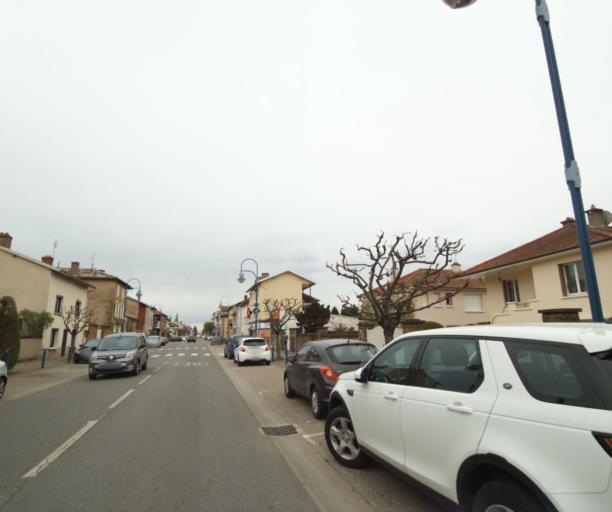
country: FR
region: Bourgogne
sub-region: Departement de Saone-et-Loire
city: Charnay-les-Macon
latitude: 46.3088
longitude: 4.8078
